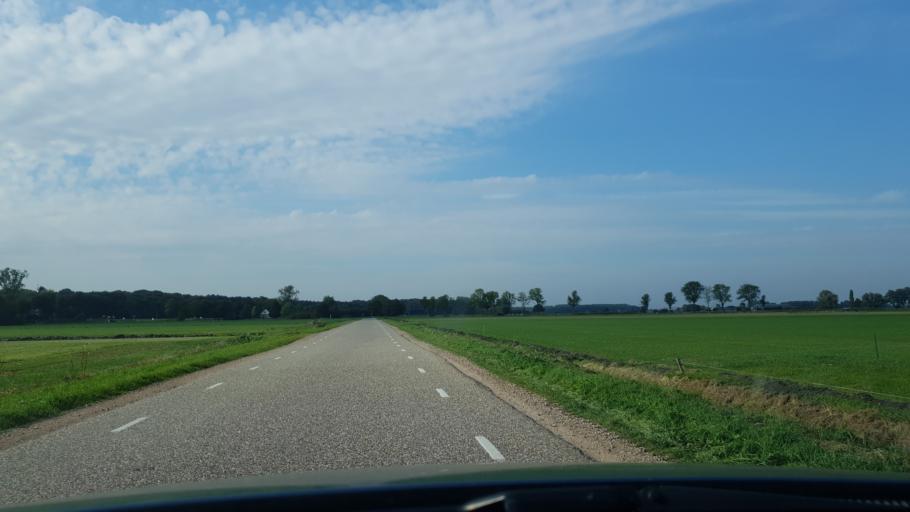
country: NL
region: Gelderland
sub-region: Gemeente Wijchen
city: Bergharen
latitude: 51.8544
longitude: 5.6861
